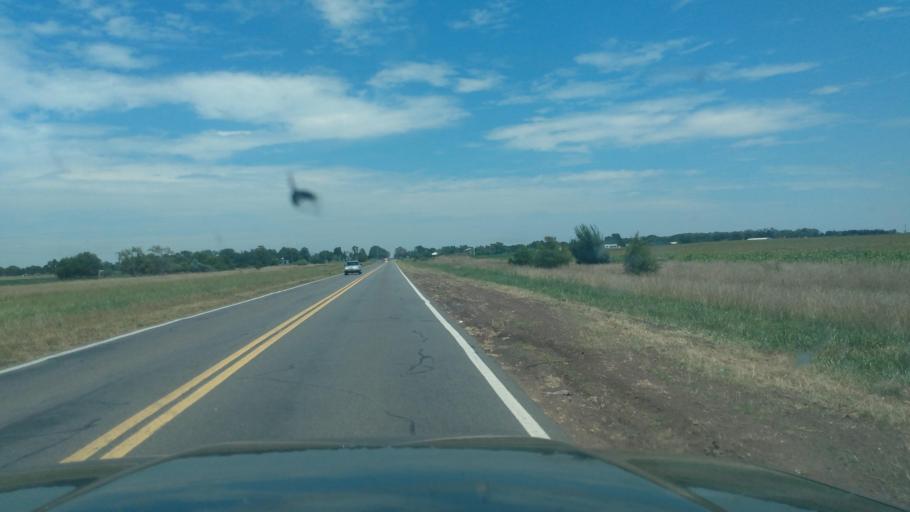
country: AR
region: Buenos Aires
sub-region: Partido de Pehuajo
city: Pehuajo
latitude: -35.8315
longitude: -61.8540
